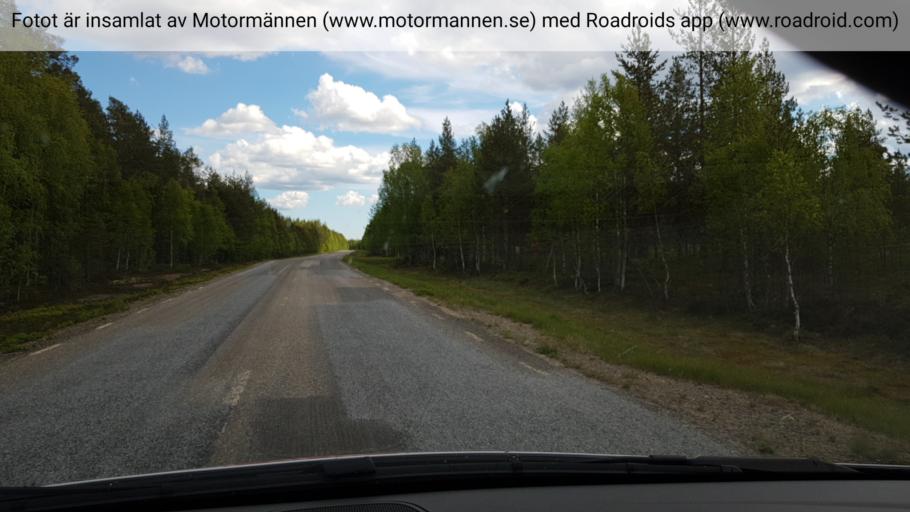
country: SE
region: Vaesterbotten
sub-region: Umea Kommun
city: Ersmark
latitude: 64.2235
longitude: 20.2931
